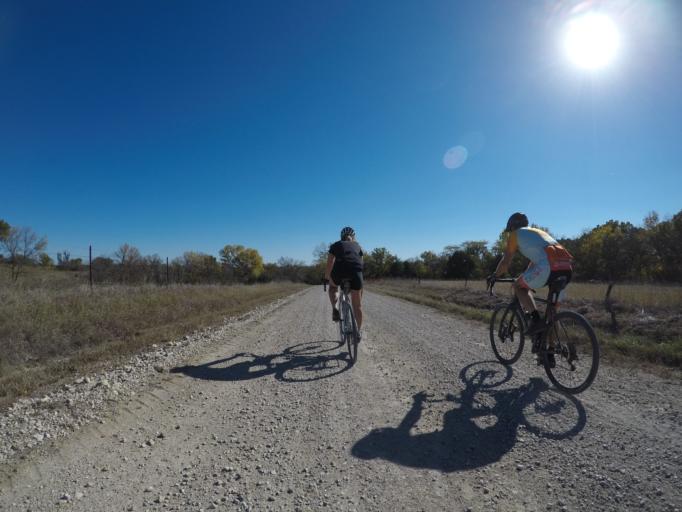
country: US
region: Kansas
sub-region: Wabaunsee County
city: Alma
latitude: 38.9474
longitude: -96.4629
